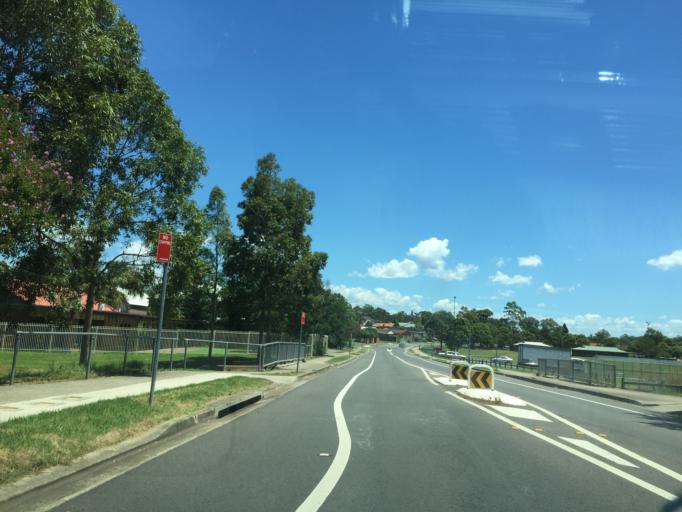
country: AU
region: New South Wales
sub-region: Blacktown
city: Mount Druitt
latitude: -33.7874
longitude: 150.8339
